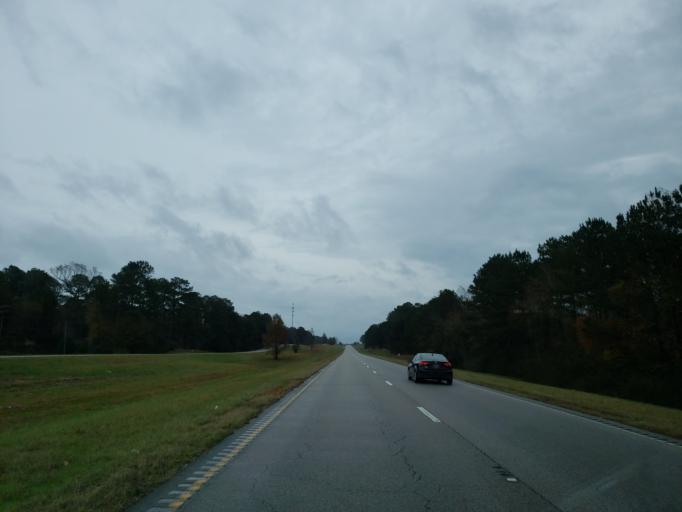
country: US
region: Mississippi
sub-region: Jones County
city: Sharon
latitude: 31.7057
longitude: -88.9336
